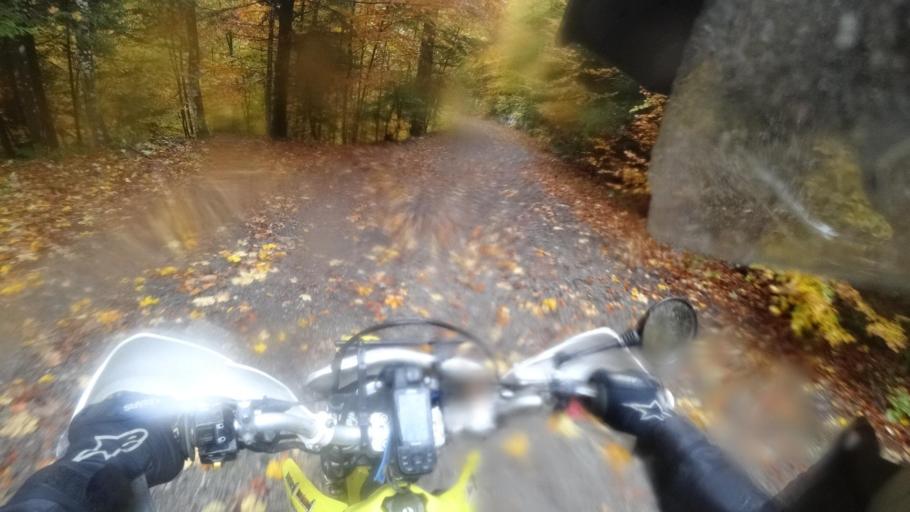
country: HR
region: Primorsko-Goranska
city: Vrbovsko
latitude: 45.3317
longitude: 15.0677
